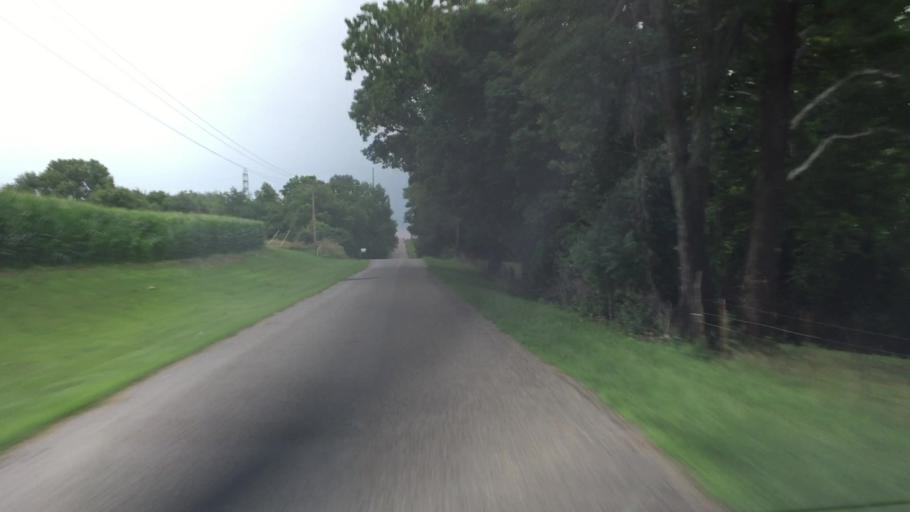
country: US
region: Illinois
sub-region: Hancock County
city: Hamilton
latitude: 40.4263
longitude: -91.3577
